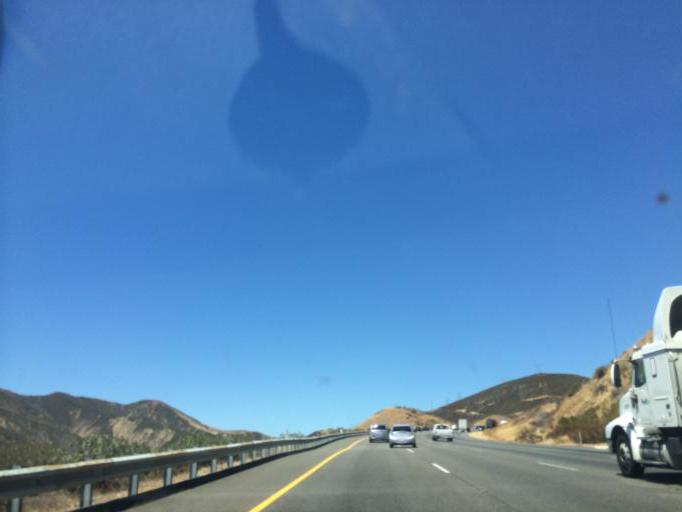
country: US
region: California
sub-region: Los Angeles County
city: Castaic
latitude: 34.5497
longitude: -118.6691
